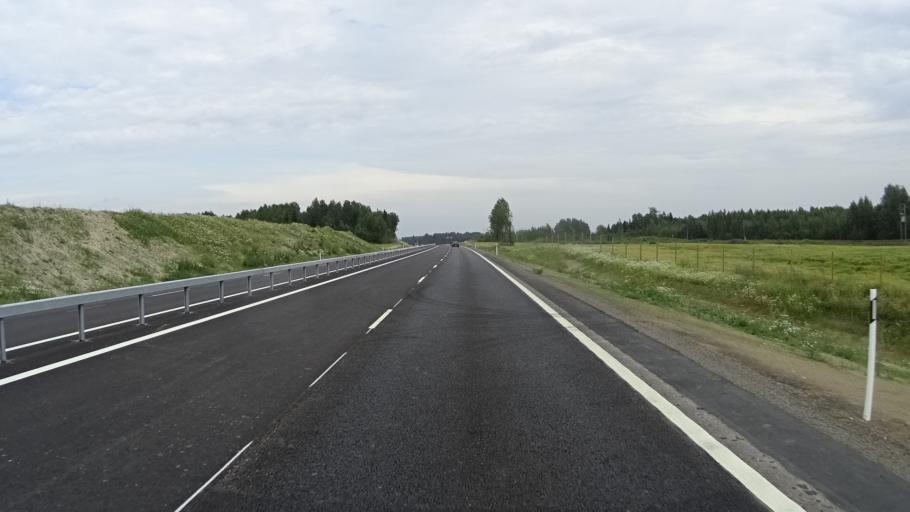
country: FI
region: South Karelia
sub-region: Lappeenranta
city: Lemi
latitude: 60.9536
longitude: 27.8176
